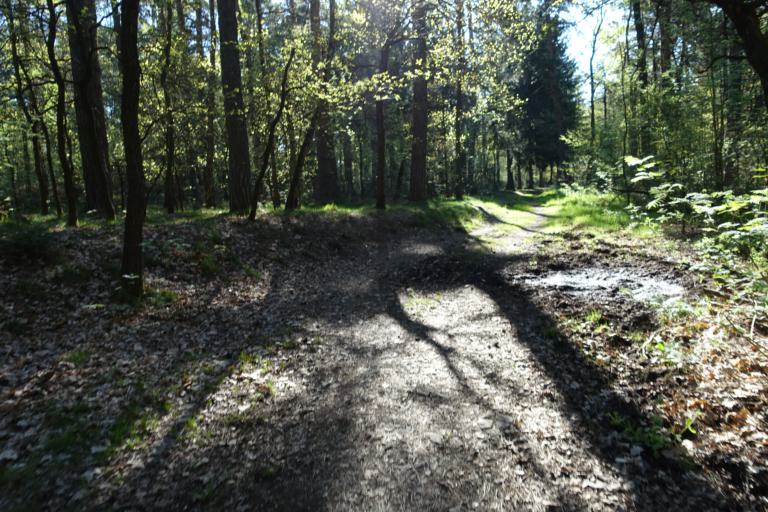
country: DE
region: Saxony
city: Freiberg
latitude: 50.8996
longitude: 13.3968
